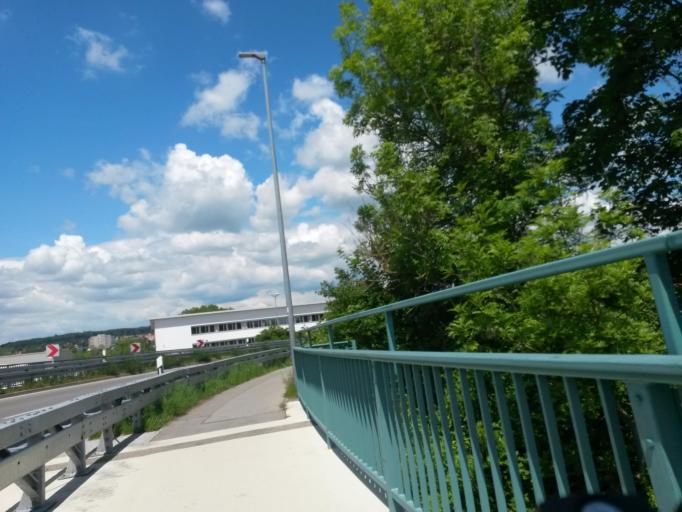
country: DE
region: Baden-Wuerttemberg
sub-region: Tuebingen Region
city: Bad Schussenried
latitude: 47.9929
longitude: 9.6654
